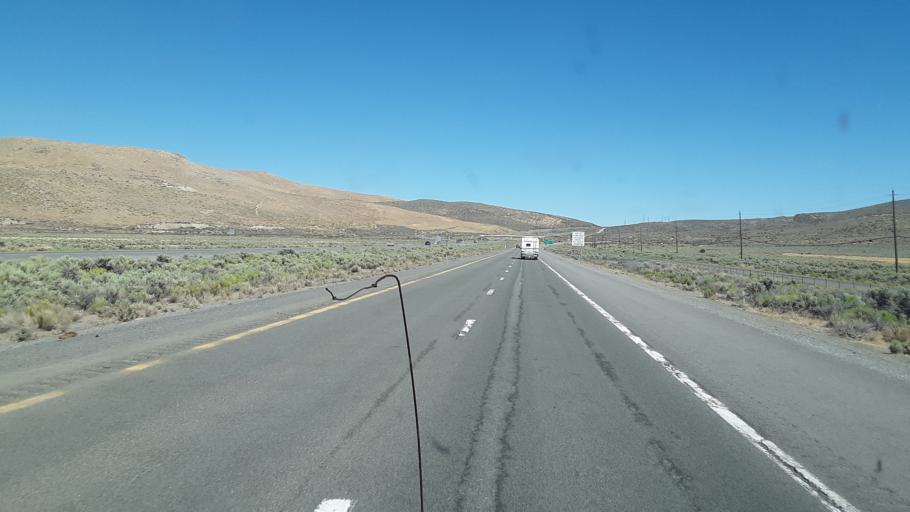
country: US
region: Nevada
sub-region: Washoe County
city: Cold Springs
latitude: 39.6478
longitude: -119.9701
